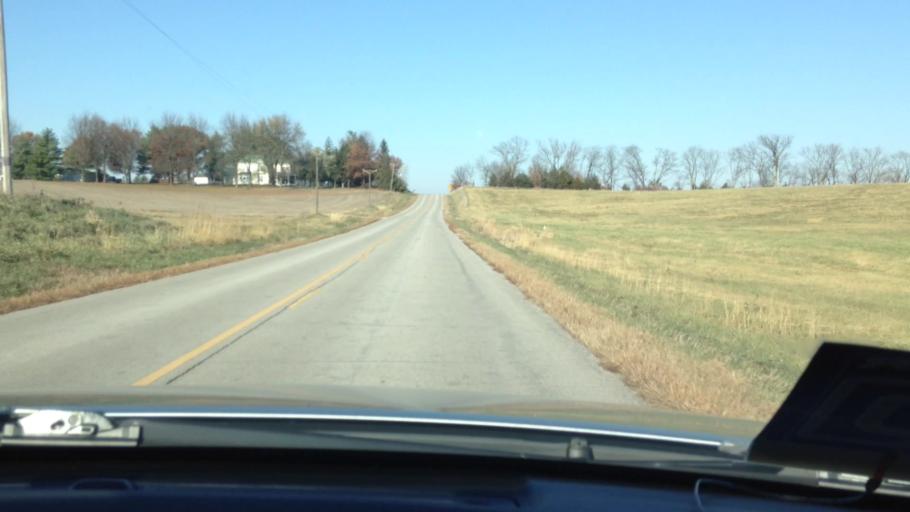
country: US
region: Missouri
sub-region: Platte County
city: Weston
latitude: 39.4401
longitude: -94.8543
